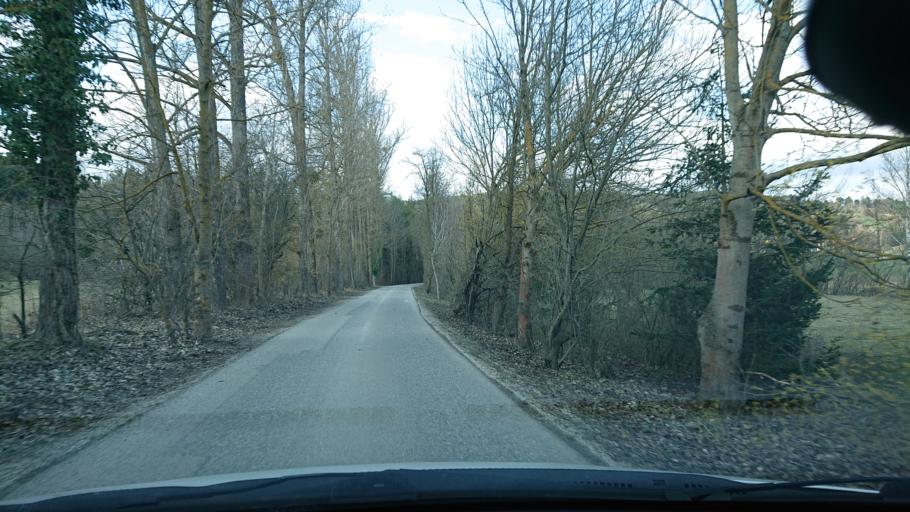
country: AT
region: Lower Austria
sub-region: Politischer Bezirk Baden
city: Pottenstein
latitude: 47.9338
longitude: 16.0818
